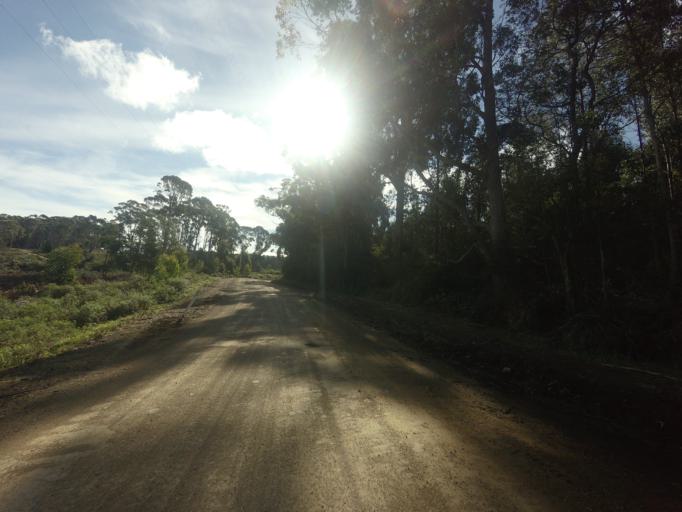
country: AU
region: Tasmania
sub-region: Clarence
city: Sandford
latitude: -43.1723
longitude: 147.7698
